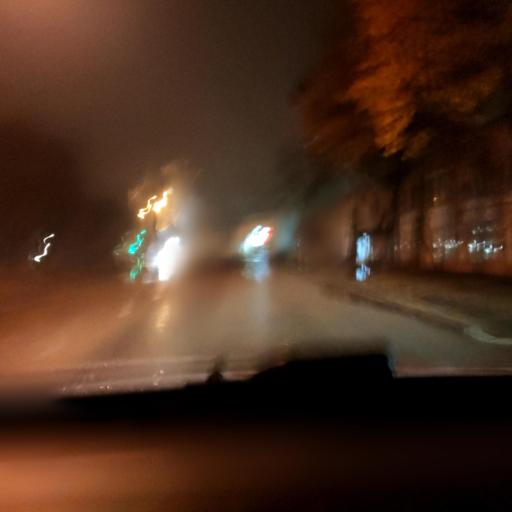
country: RU
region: Voronezj
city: Voronezh
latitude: 51.6251
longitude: 39.1765
